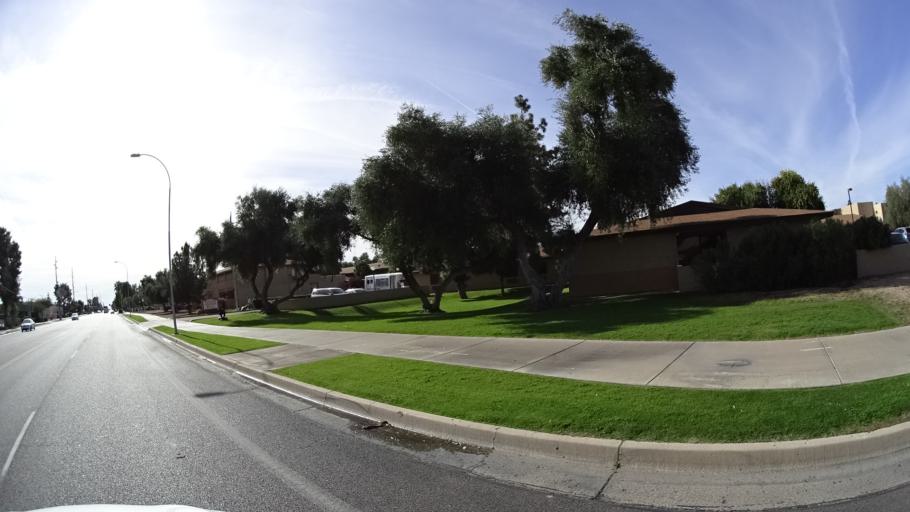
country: US
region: Arizona
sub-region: Maricopa County
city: Guadalupe
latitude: 33.3670
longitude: -111.9286
